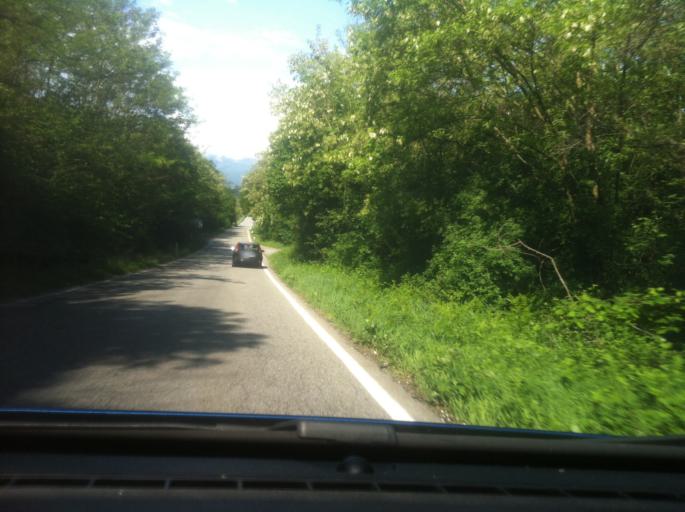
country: IT
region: Piedmont
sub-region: Provincia di Torino
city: Torre Canavese
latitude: 45.3937
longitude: 7.7527
